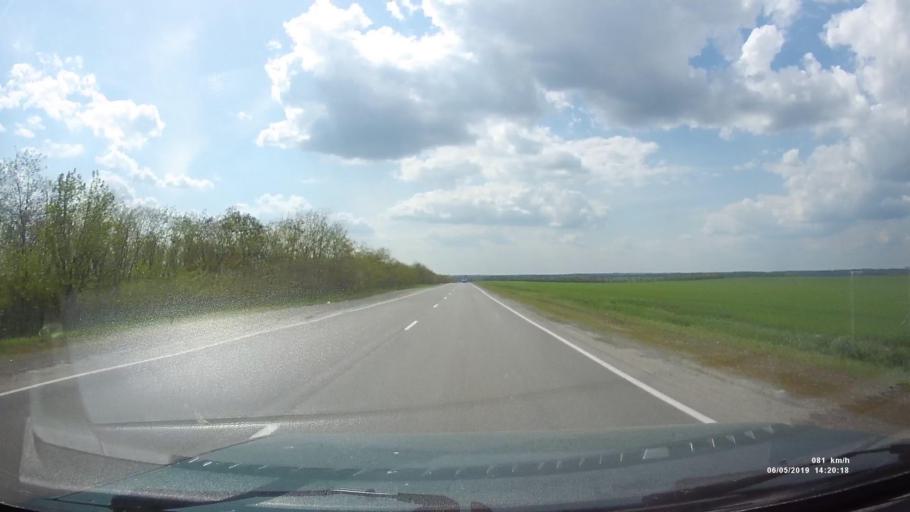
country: RU
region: Rostov
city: Kamenolomni
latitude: 47.6323
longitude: 40.2161
